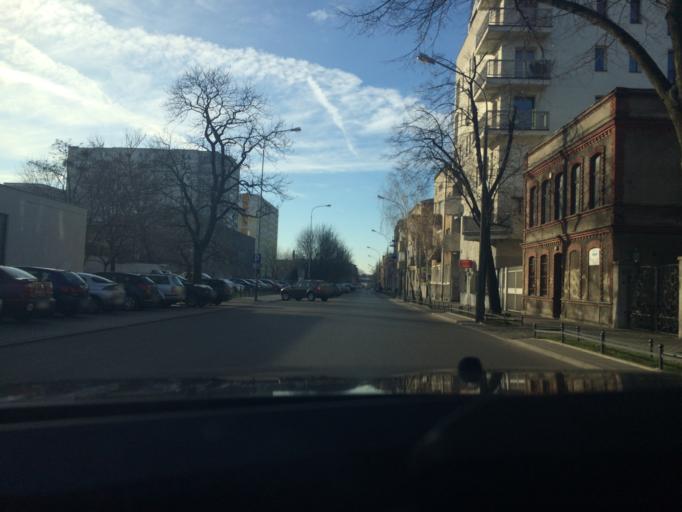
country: PL
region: Lodz Voivodeship
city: Lodz
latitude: 51.7608
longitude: 19.4417
